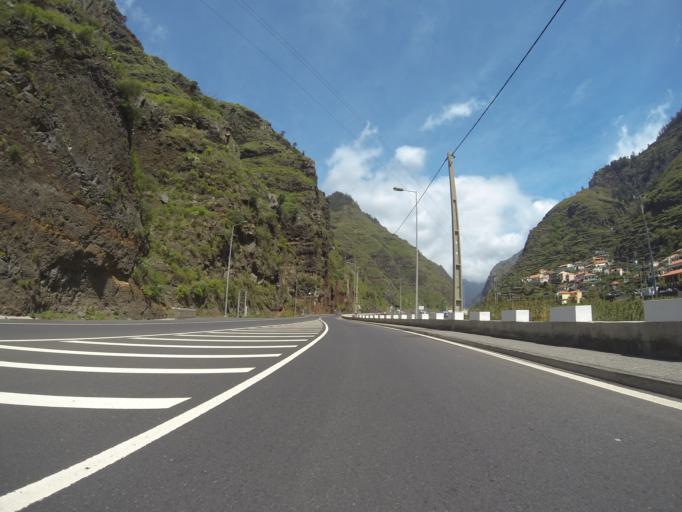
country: PT
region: Madeira
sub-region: Ribeira Brava
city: Campanario
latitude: 32.6860
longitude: -17.0513
